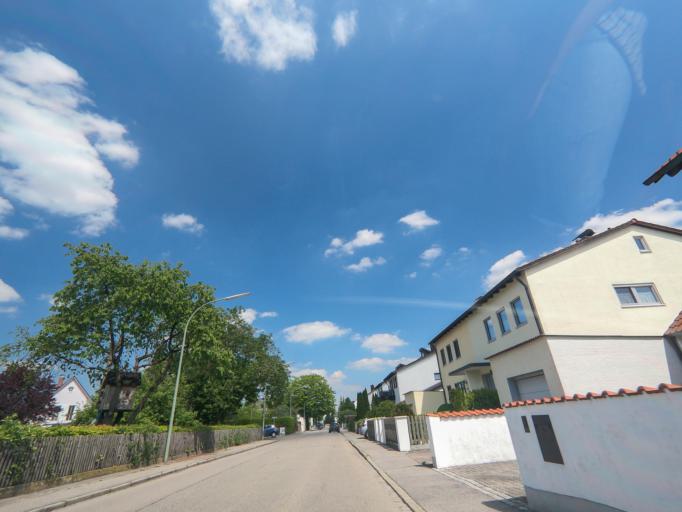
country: DE
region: Bavaria
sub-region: Lower Bavaria
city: Landshut
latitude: 48.5468
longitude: 12.1695
